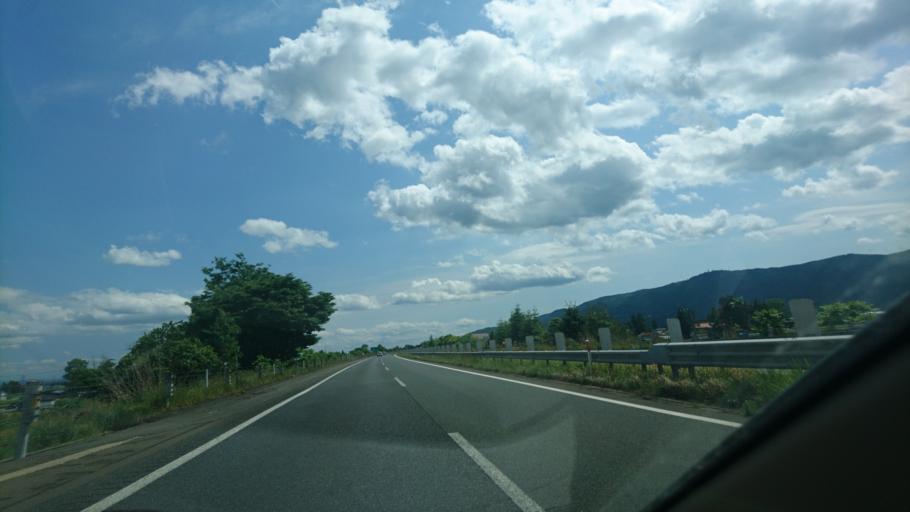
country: JP
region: Iwate
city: Morioka-shi
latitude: 39.5685
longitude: 141.1203
